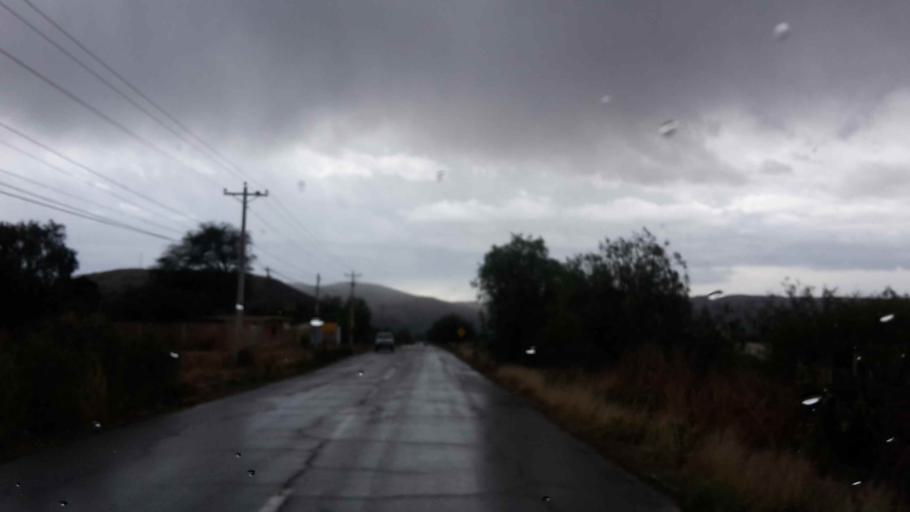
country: BO
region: Cochabamba
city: Tarata
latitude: -17.5566
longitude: -66.0880
